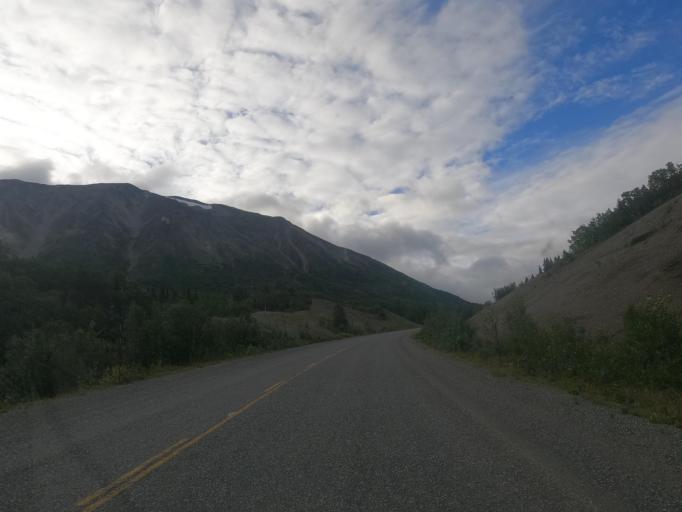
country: CA
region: Yukon
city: Haines Junction
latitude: 60.1019
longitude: -136.9155
